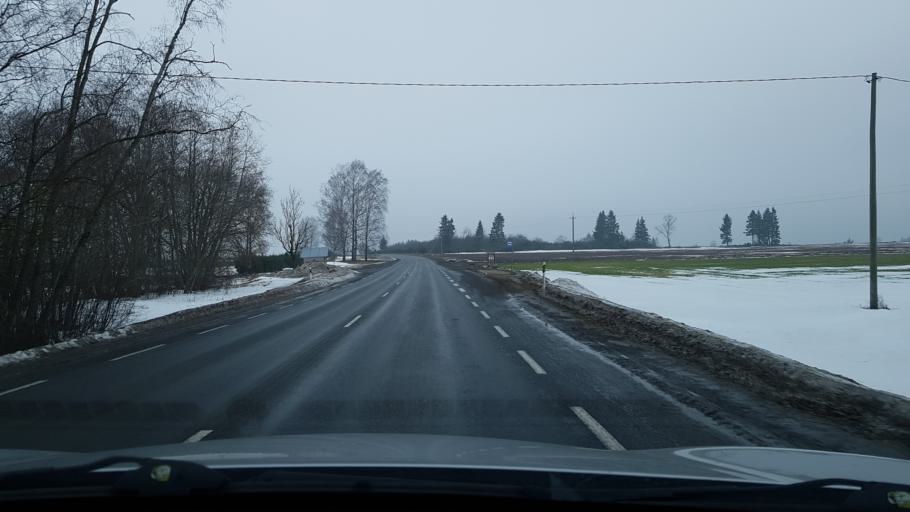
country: EE
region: Viljandimaa
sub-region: Viiratsi vald
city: Viiratsi
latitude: 58.2506
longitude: 25.8375
